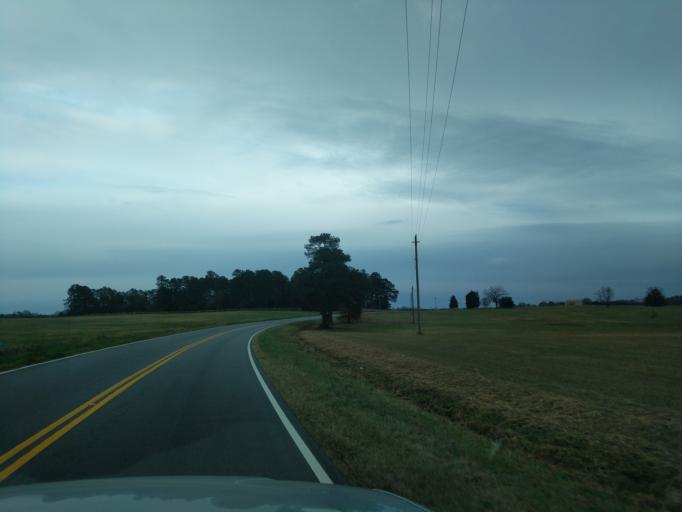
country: US
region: South Carolina
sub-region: Laurens County
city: Laurens
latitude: 34.3731
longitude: -81.9963
